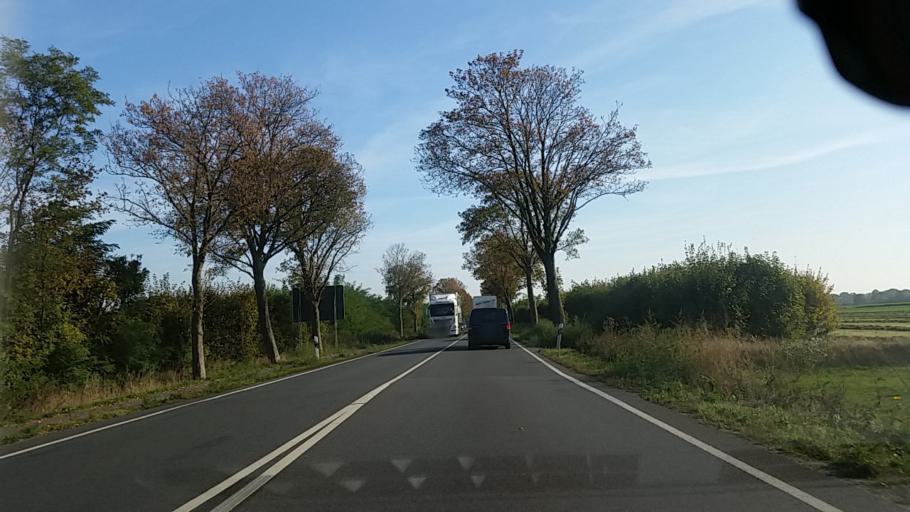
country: DE
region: Lower Saxony
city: Klein Schwulper
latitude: 52.3453
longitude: 10.4115
